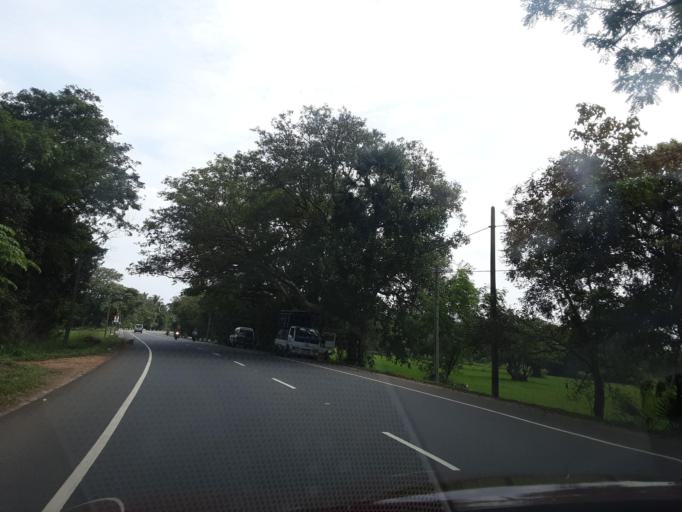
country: LK
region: North Central
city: Anuradhapura
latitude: 8.5137
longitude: 80.5043
